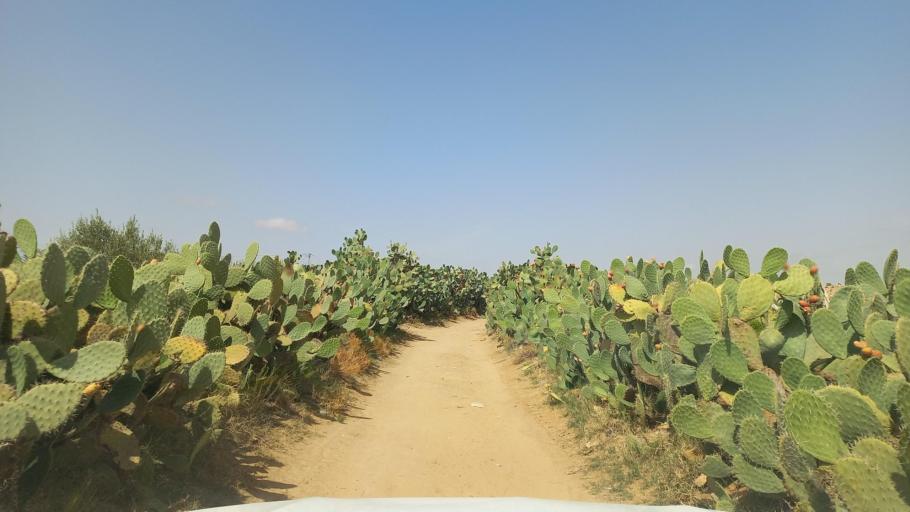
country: TN
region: Al Qasrayn
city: Sbiba
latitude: 35.3872
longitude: 8.9608
